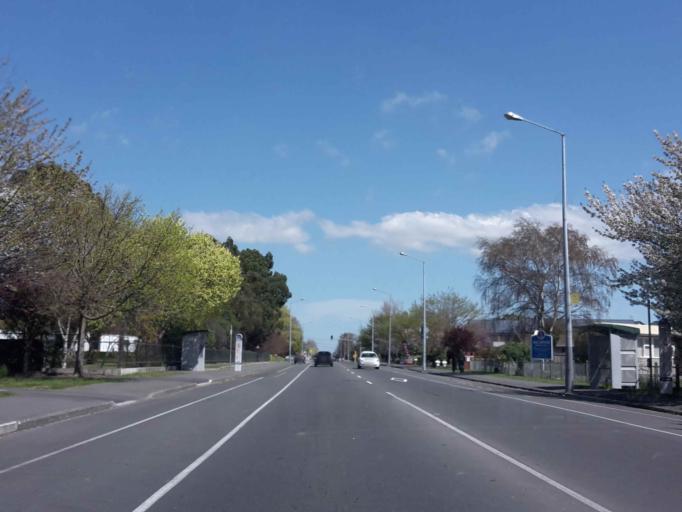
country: NZ
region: Canterbury
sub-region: Christchurch City
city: Christchurch
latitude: -43.5336
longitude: 172.5647
